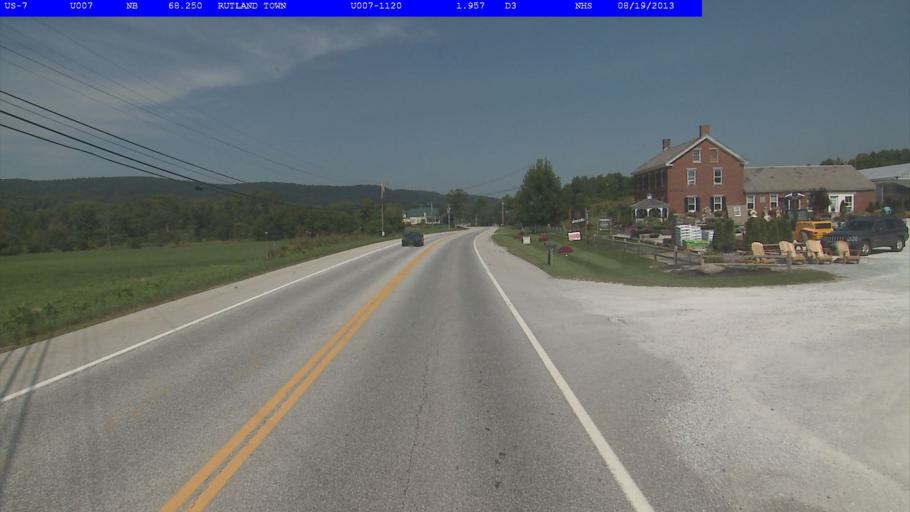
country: US
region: Vermont
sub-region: Rutland County
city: Rutland
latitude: 43.6407
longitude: -72.9790
